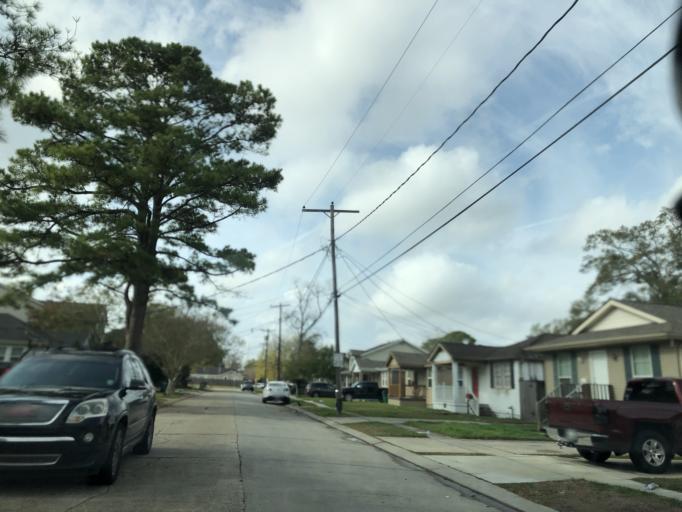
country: US
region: Louisiana
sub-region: Jefferson Parish
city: Metairie Terrace
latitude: 29.9777
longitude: -90.1682
